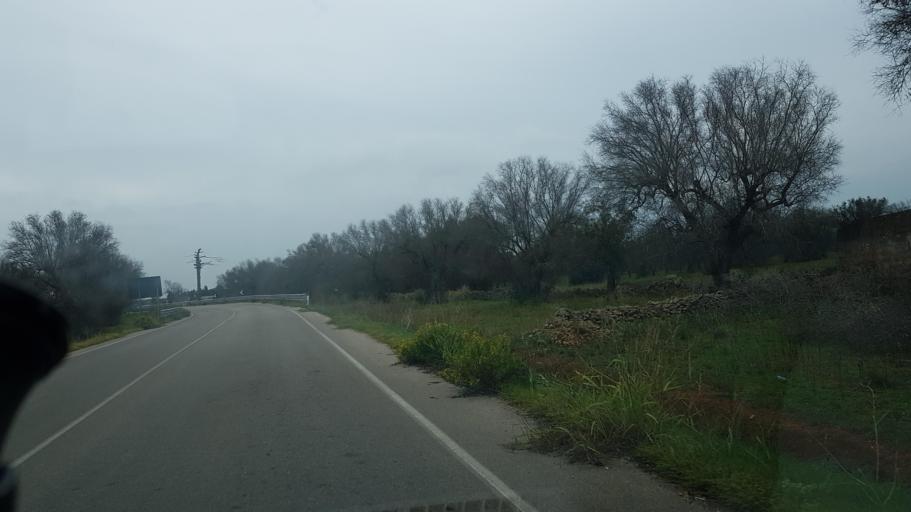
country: IT
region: Apulia
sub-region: Provincia di Brindisi
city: San Pietro Vernotico
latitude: 40.4868
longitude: 18.0107
